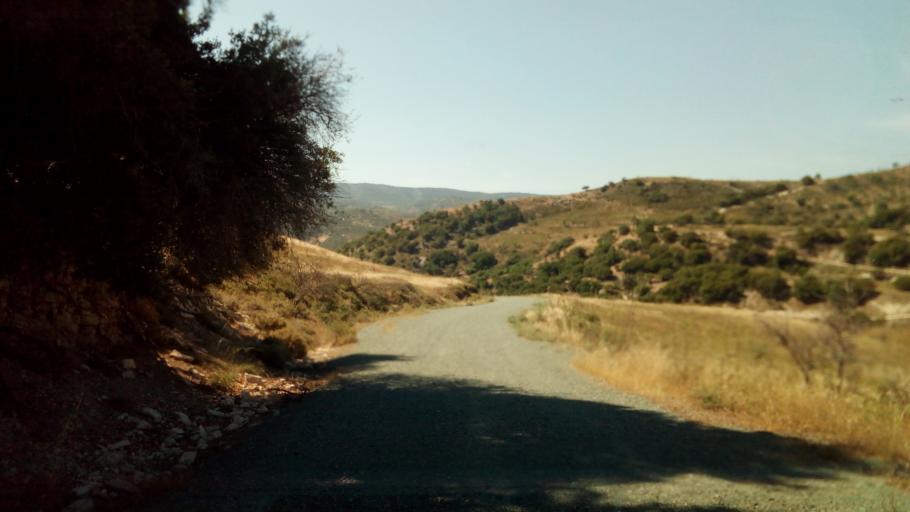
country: CY
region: Limassol
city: Pachna
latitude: 34.8129
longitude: 32.7092
